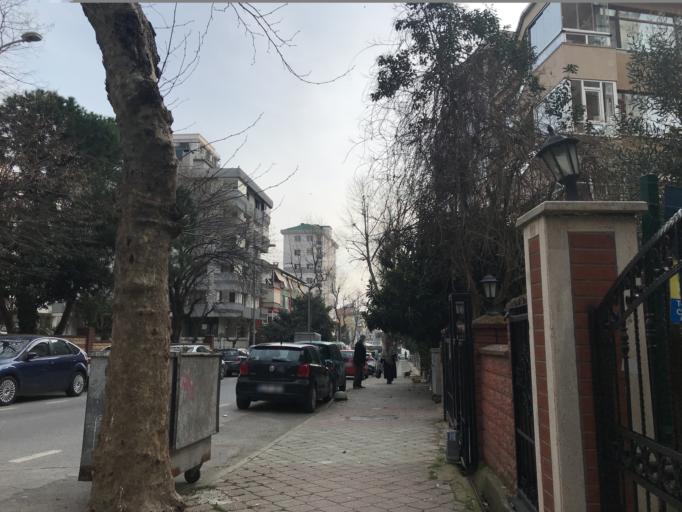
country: TR
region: Istanbul
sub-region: Atasehir
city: Atasehir
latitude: 40.9575
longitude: 29.0920
